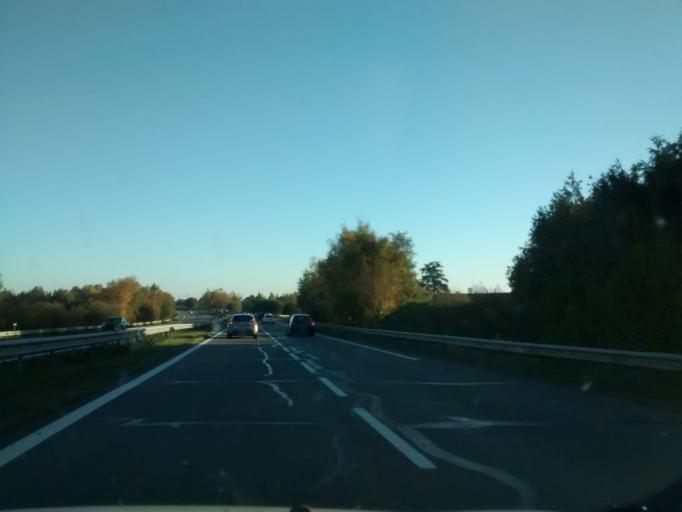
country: FR
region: Brittany
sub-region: Departement d'Ille-et-Vilaine
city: Quedillac
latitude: 48.2249
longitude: -2.1143
